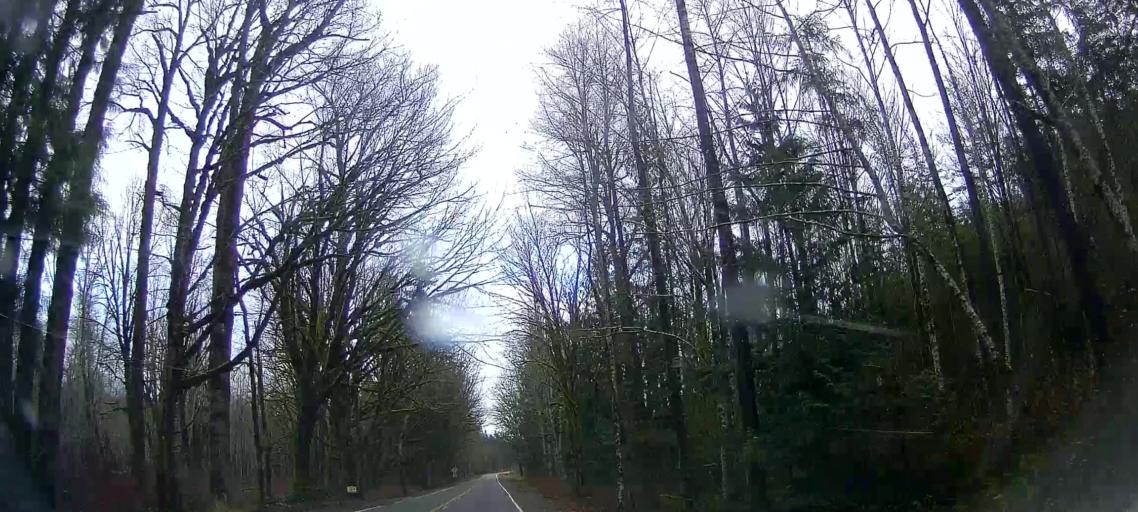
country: US
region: Washington
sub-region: Skagit County
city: Sedro-Woolley
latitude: 48.5123
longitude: -122.0031
